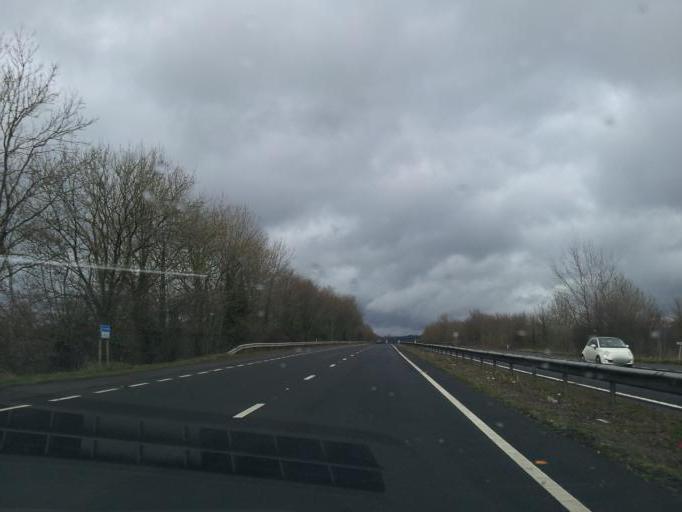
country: GB
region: England
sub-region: Somerset
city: Wincanton
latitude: 51.0568
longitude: -2.3927
